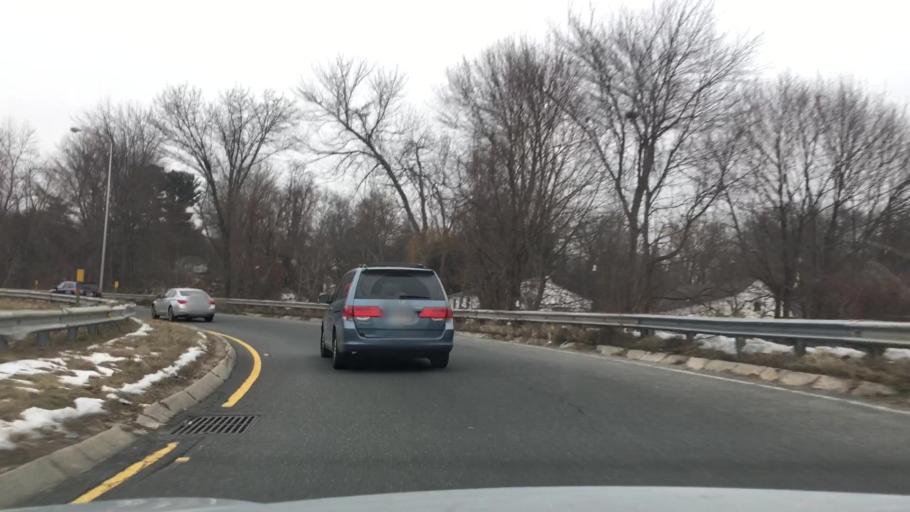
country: US
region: Massachusetts
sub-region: Hampden County
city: Chicopee
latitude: 42.1590
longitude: -72.6371
